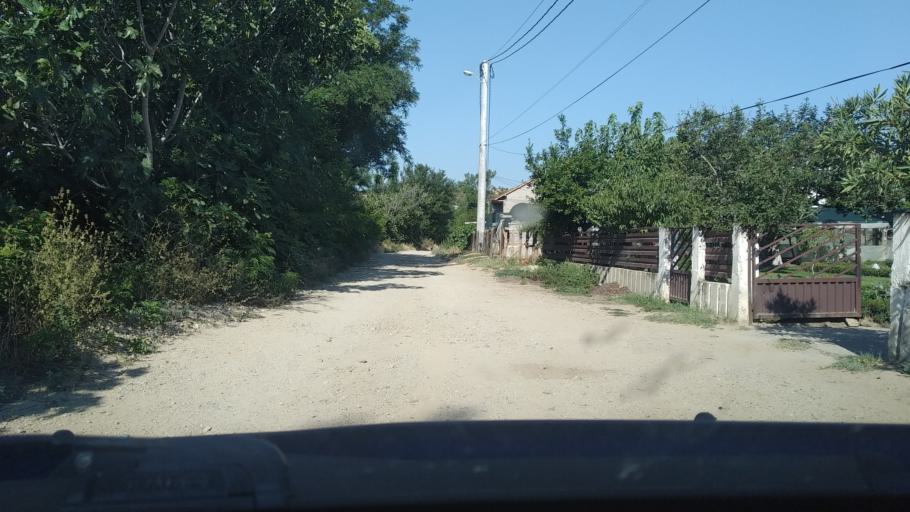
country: MK
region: Bogdanci
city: Bogdanci
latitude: 41.2027
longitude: 22.5687
